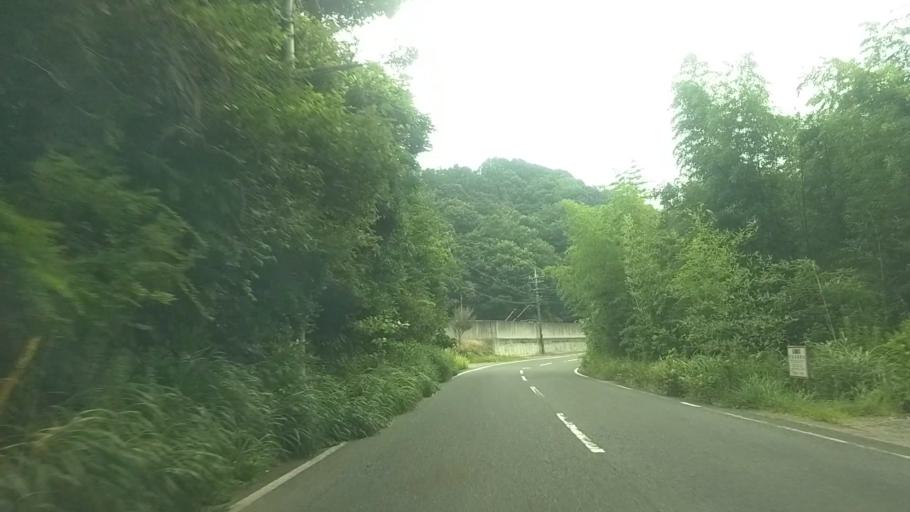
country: JP
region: Chiba
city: Kimitsu
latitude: 35.2389
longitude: 139.9862
